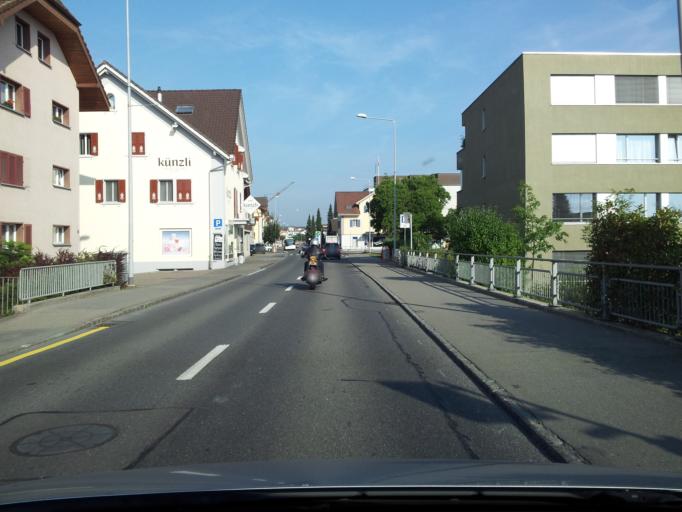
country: CH
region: Lucerne
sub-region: Sursee District
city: Nottwil
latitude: 47.1353
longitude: 8.1373
